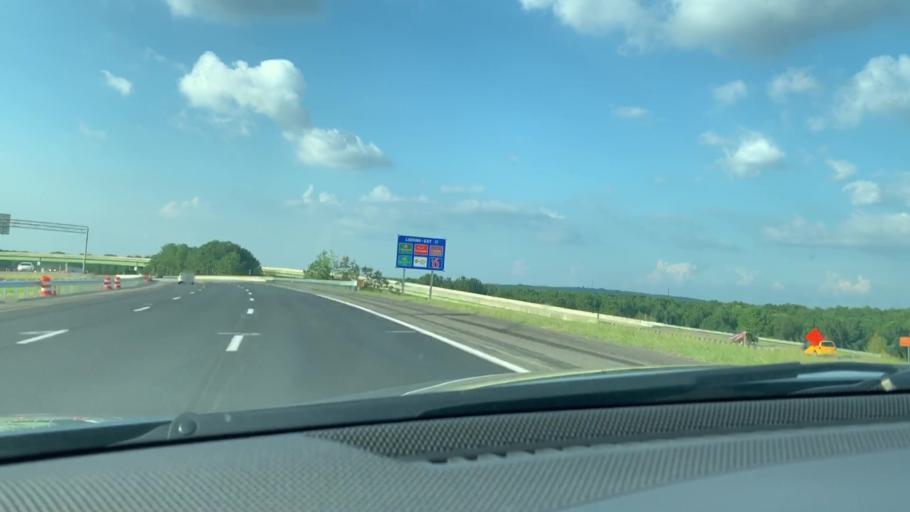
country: US
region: South Carolina
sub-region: Richland County
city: Woodfield
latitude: 34.0661
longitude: -80.9217
